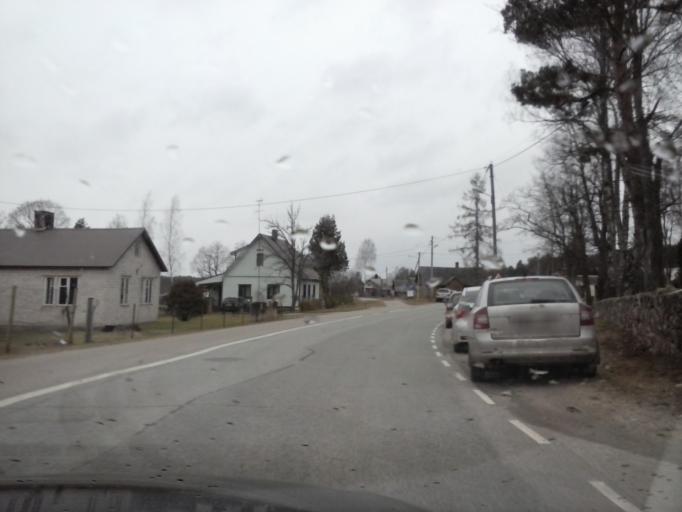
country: RU
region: Pskov
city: Pechory
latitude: 57.9595
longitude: 27.6299
